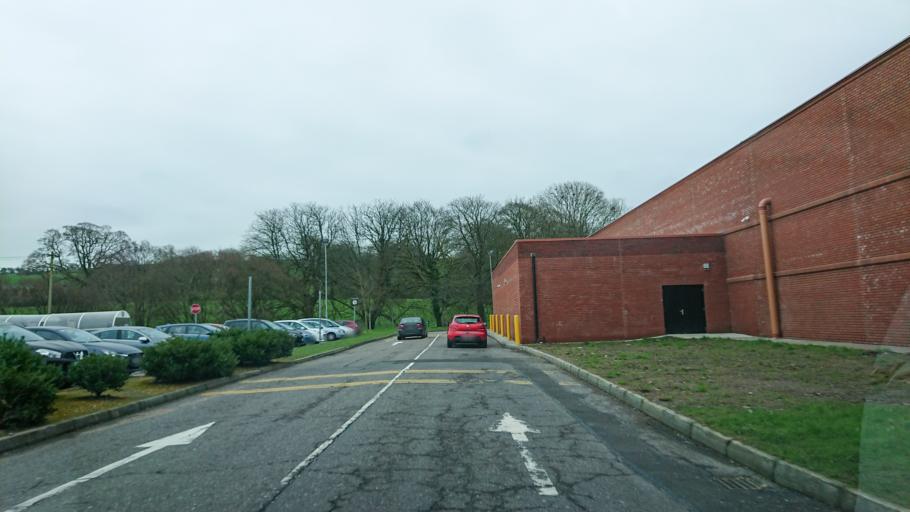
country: IE
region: Munster
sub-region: County Cork
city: Cork
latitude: 51.8739
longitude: -8.5198
